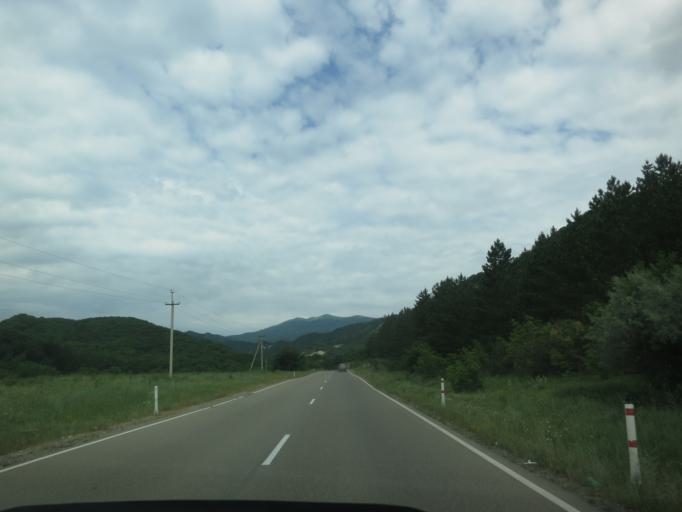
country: GE
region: Kakheti
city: Sagarejo
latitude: 41.8015
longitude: 45.1549
